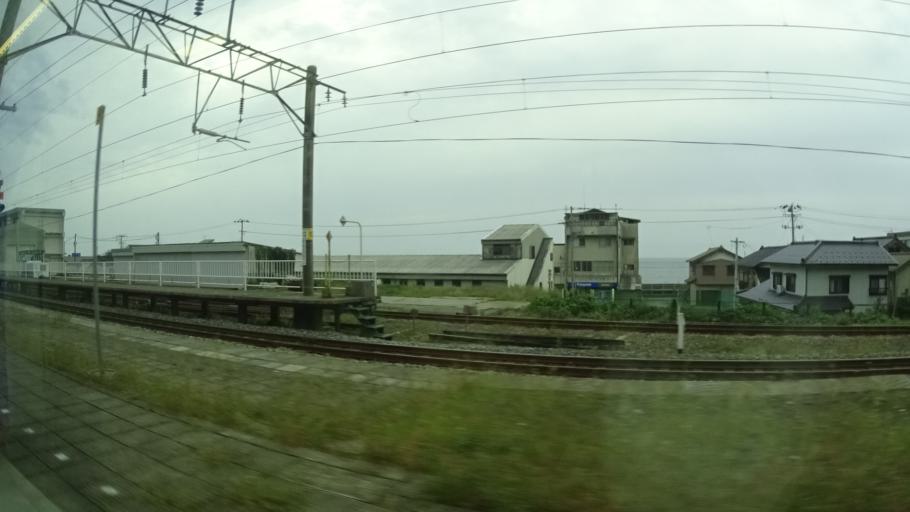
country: JP
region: Yamagata
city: Tsuruoka
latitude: 38.6256
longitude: 139.5887
